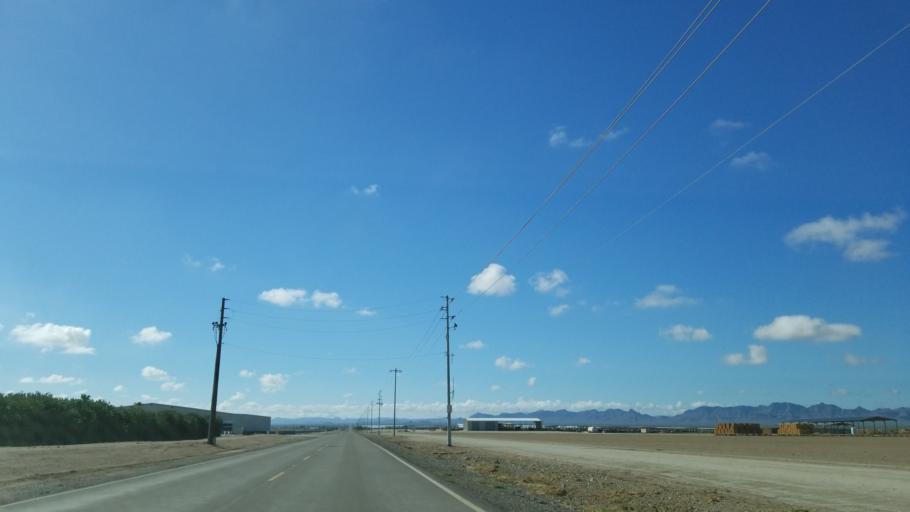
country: US
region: Arizona
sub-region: La Paz County
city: Salome
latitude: 33.6931
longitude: -113.7672
